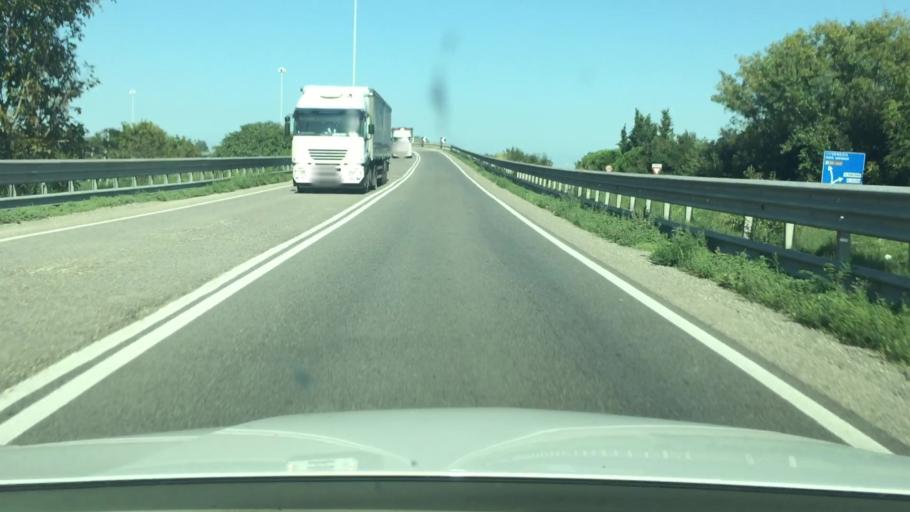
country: IT
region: Emilia-Romagna
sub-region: Provincia di Ravenna
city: Ravenna
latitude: 44.4557
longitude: 12.2061
